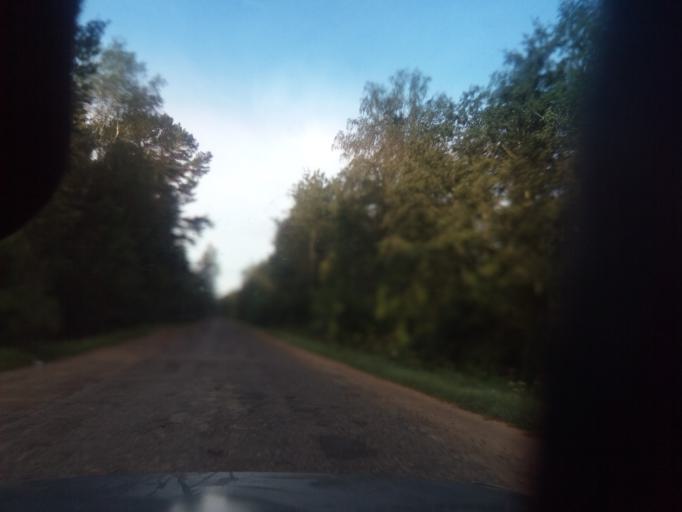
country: BY
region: Vitebsk
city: Dzisna
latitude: 55.6330
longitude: 28.3036
